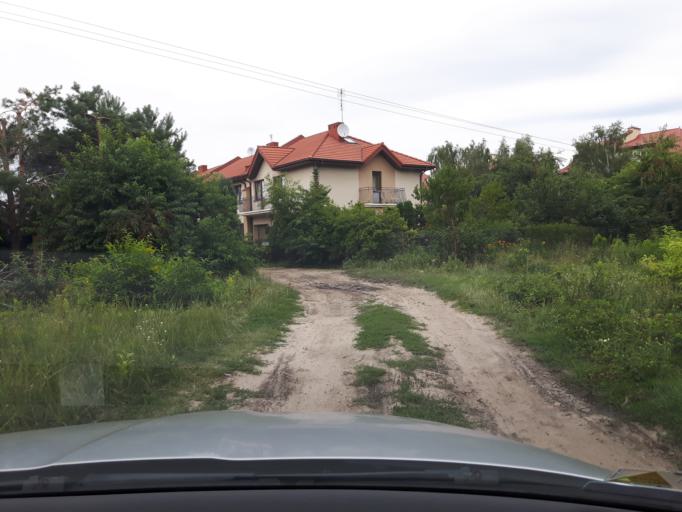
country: PL
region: Masovian Voivodeship
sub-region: Powiat wolominski
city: Zabki
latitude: 52.2764
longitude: 21.1240
